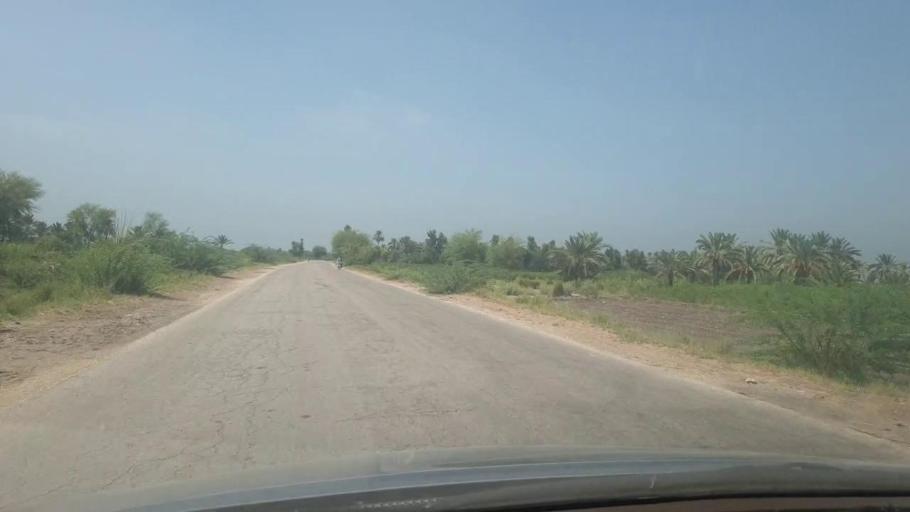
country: PK
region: Sindh
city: Ranipur
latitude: 27.2573
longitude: 68.5877
